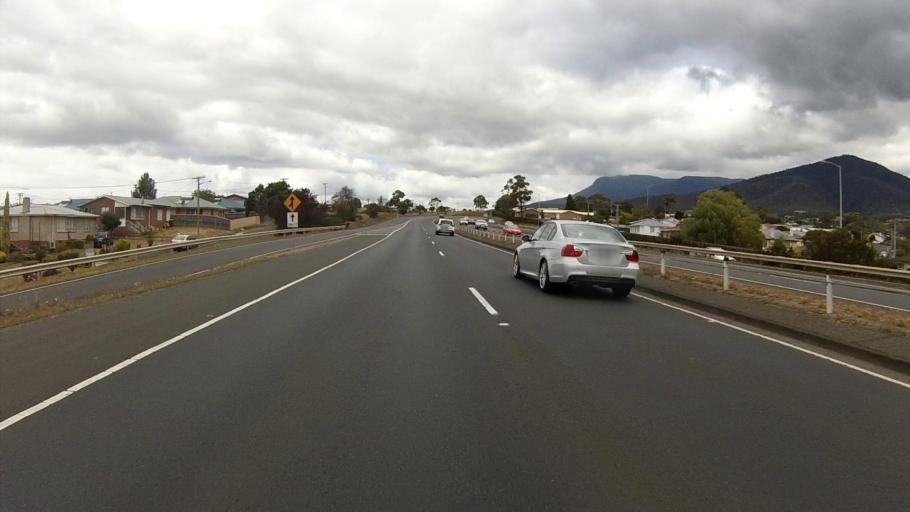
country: AU
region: Tasmania
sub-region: Glenorchy
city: Claremont
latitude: -42.7999
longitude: 147.2490
